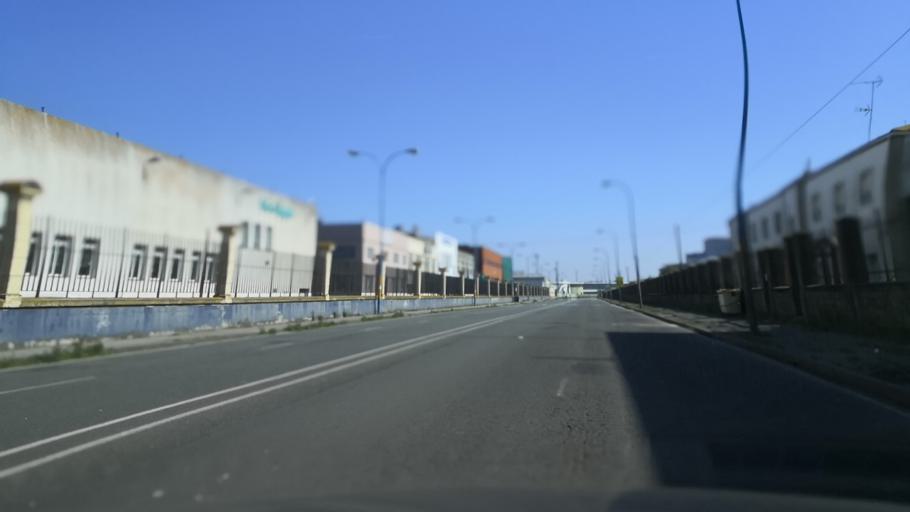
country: ES
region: Galicia
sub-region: Provincia da Coruna
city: A Coruna
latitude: 43.3572
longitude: -8.3950
